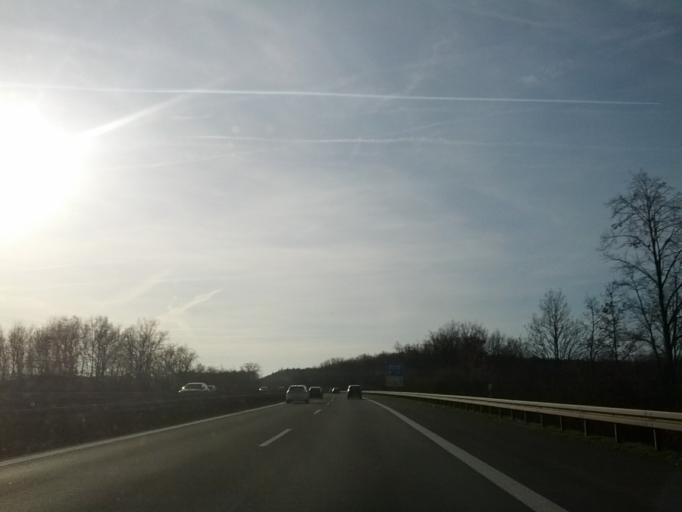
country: DE
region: Bavaria
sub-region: Regierungsbezirk Unterfranken
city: Arnstein
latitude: 49.9337
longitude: 10.0016
